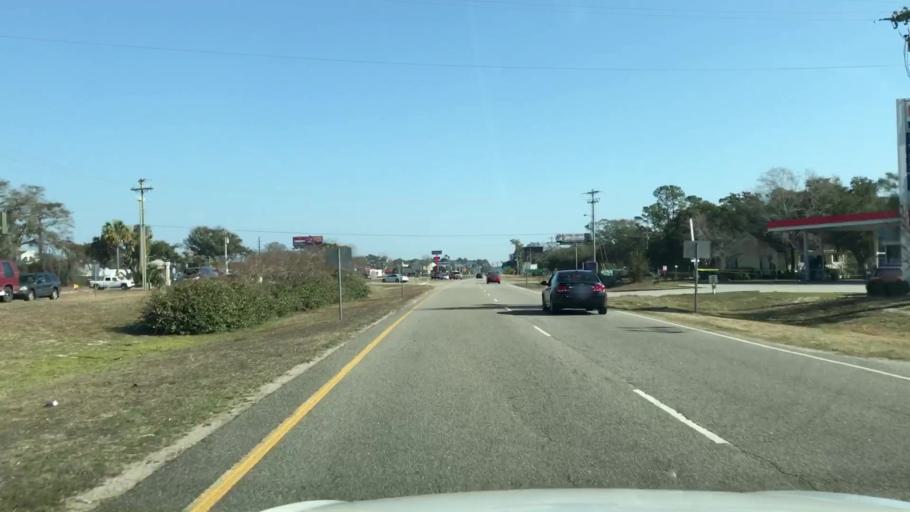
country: US
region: South Carolina
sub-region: Horry County
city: Garden City
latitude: 33.5755
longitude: -79.0267
